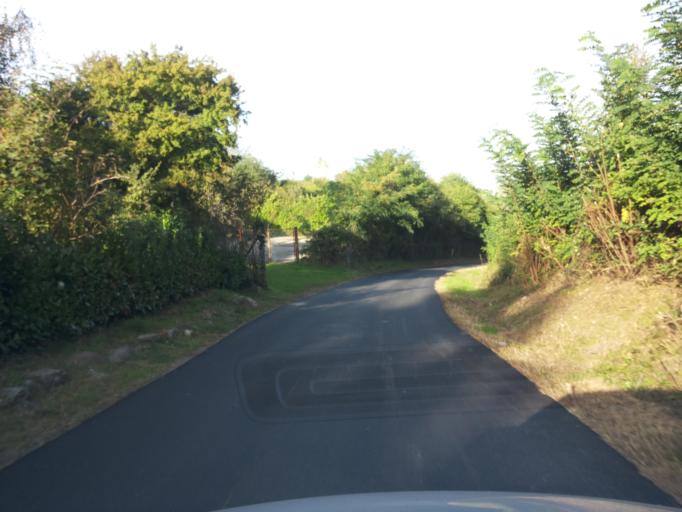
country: IT
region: Piedmont
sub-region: Provincia di Biella
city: Dorzano
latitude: 45.4436
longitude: 8.0923
